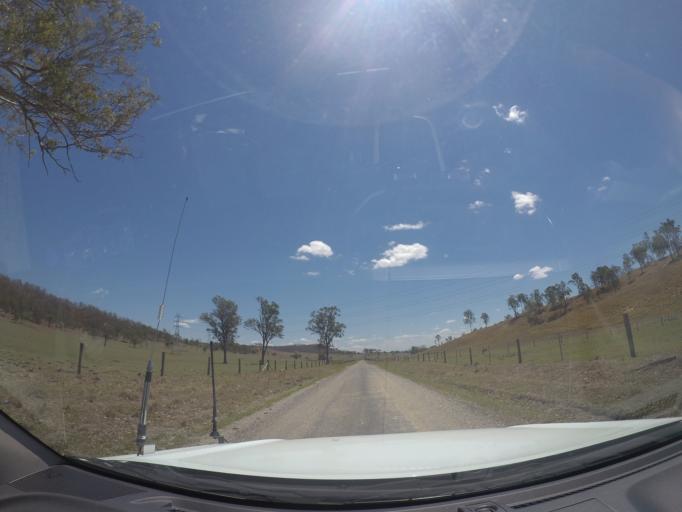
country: AU
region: Queensland
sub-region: Ipswich
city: Redbank Plains
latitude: -27.7515
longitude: 152.8331
